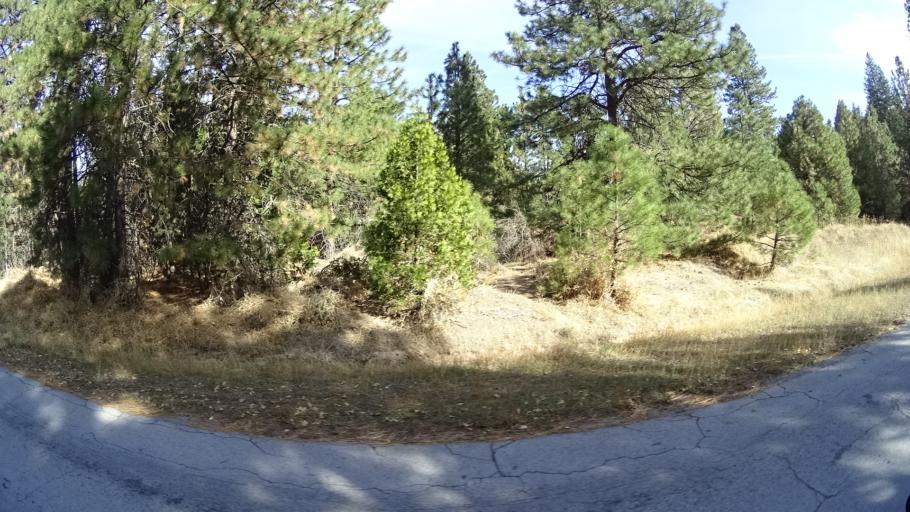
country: US
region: California
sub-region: Siskiyou County
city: Weed
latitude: 41.4314
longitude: -122.4135
